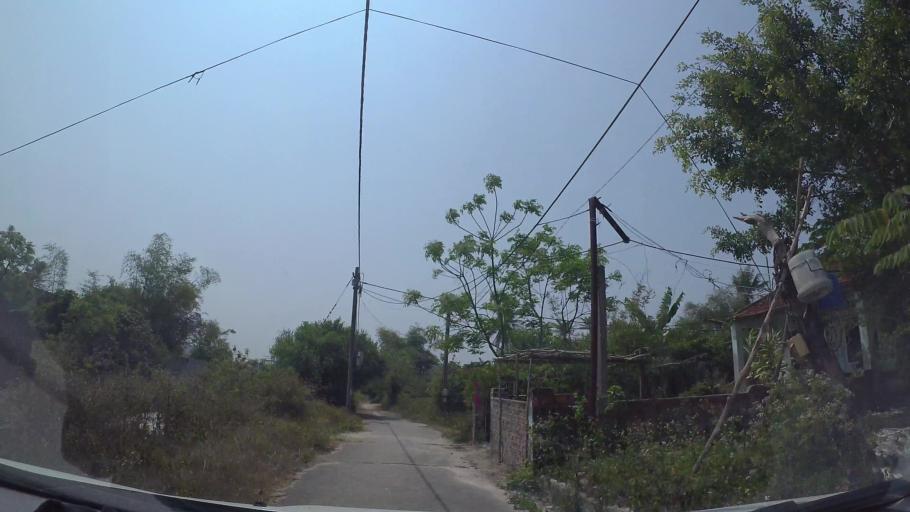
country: VN
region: Da Nang
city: Ngu Hanh Son
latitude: 15.9891
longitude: 108.2659
